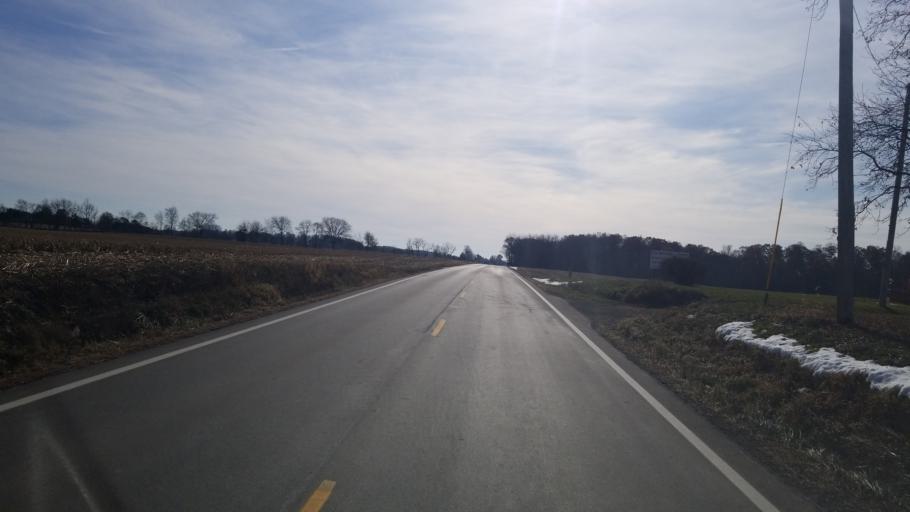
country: US
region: Ohio
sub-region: Huron County
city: Norwalk
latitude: 41.1992
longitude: -82.6358
